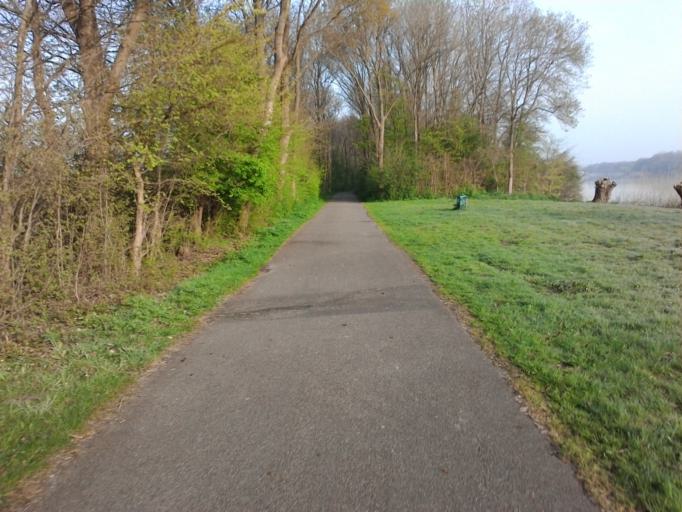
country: NL
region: Utrecht
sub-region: Stichtse Vecht
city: Maarssen
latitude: 52.1359
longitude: 5.0940
